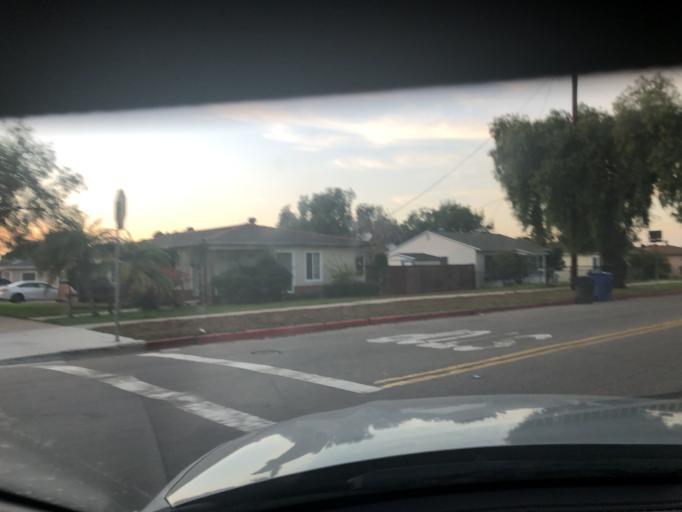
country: US
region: California
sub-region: San Diego County
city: Chula Vista
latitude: 32.6437
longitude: -117.0716
